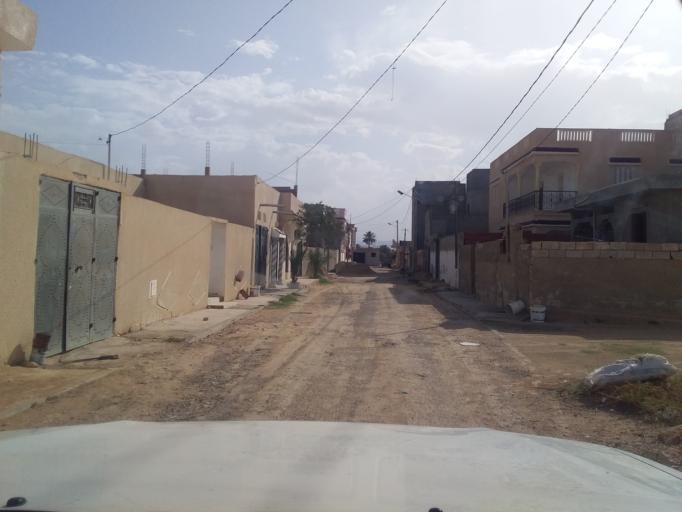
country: TN
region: Qabis
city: Matmata
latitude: 33.6164
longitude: 10.2814
